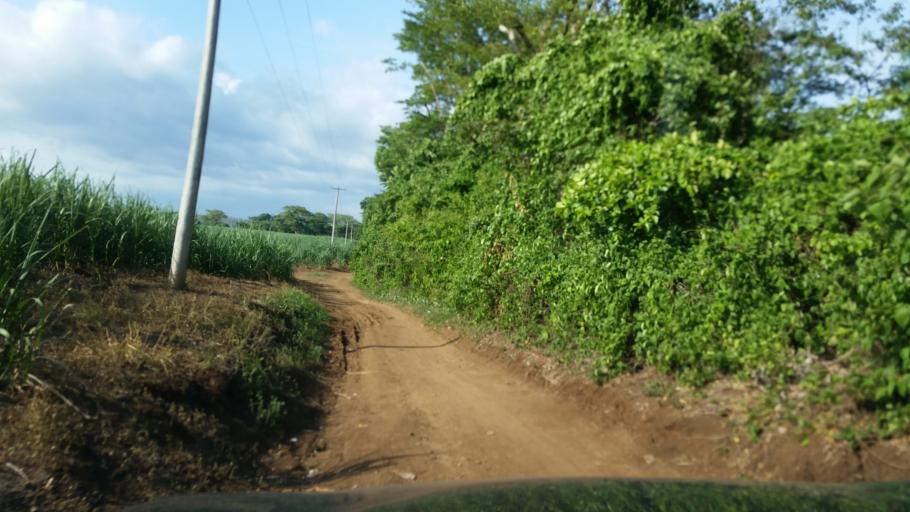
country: NI
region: Managua
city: Masachapa
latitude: 11.7930
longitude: -86.5091
